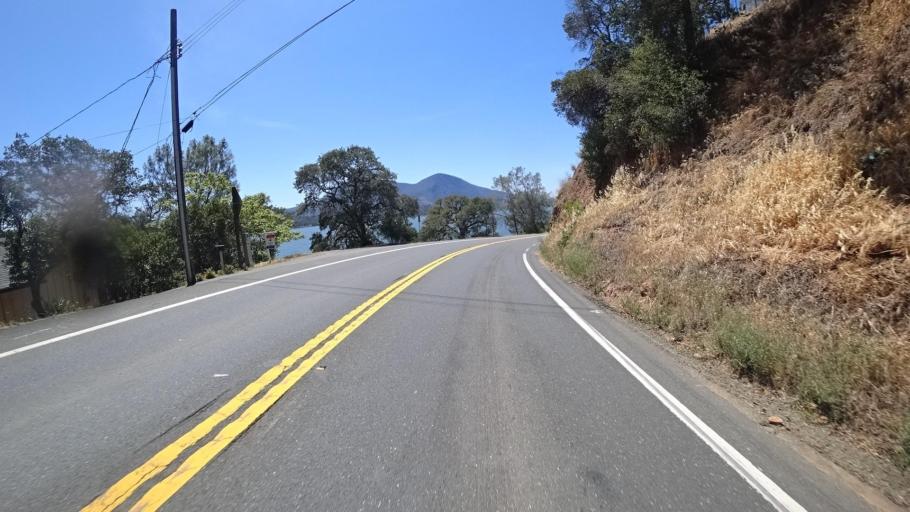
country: US
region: California
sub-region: Lake County
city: Clearlake Oaks
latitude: 39.0204
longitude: -122.6939
